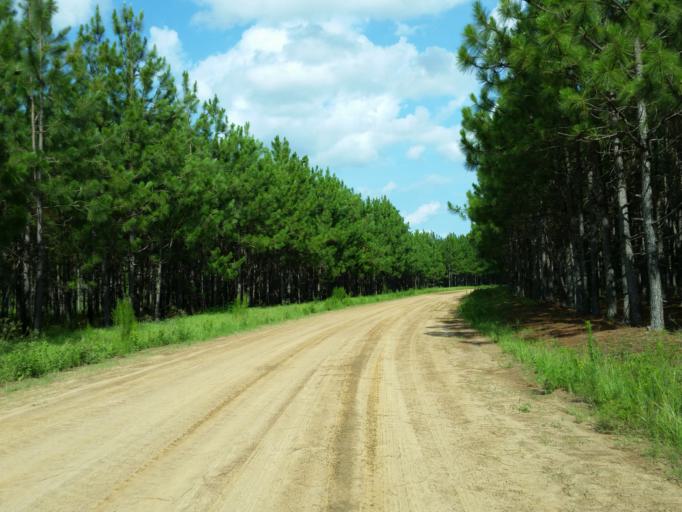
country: US
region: Georgia
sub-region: Lee County
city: Leesburg
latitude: 31.7666
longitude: -84.0359
